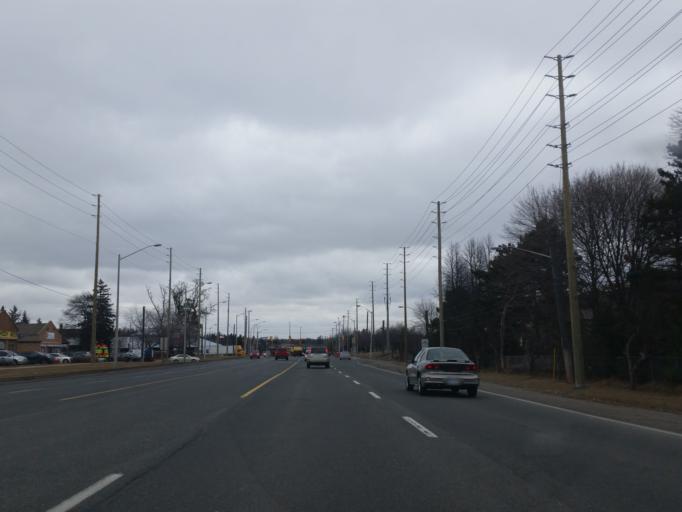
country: CA
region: Ontario
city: Ajax
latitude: 43.8463
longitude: -79.0763
